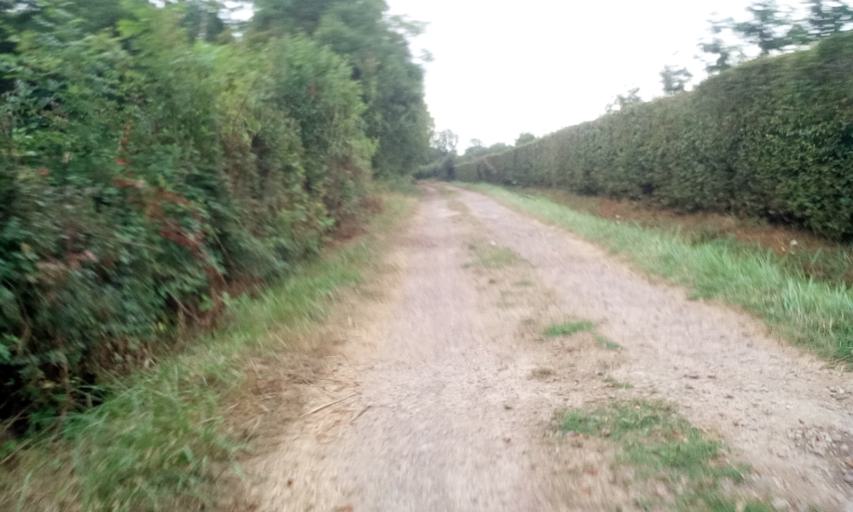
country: FR
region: Lower Normandy
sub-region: Departement du Calvados
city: Sannerville
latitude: 49.1854
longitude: -0.2077
